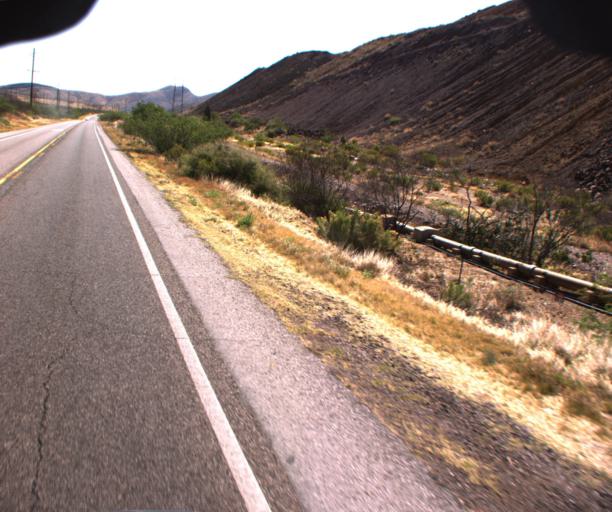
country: US
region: Arizona
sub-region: Cochise County
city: Bisbee
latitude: 31.4284
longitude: -109.8800
